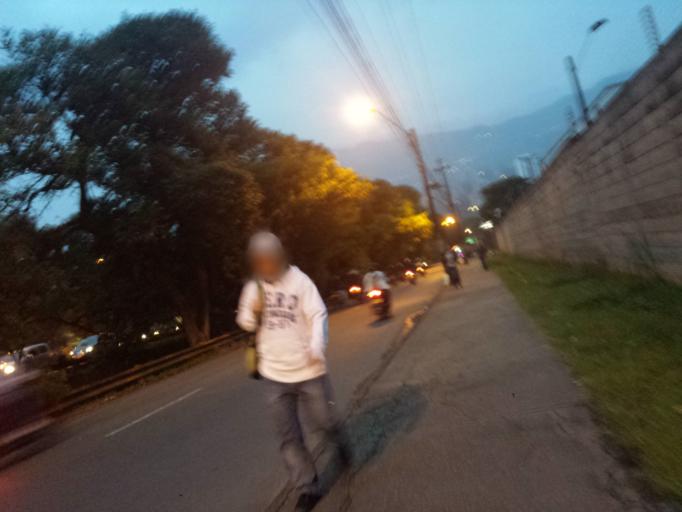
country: CO
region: Antioquia
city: Itagui
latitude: 6.1965
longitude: -75.5865
